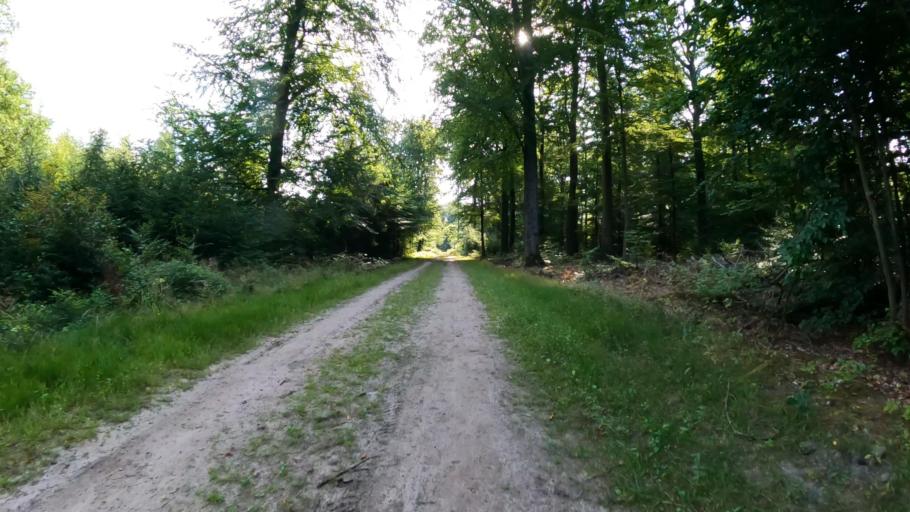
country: DE
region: Schleswig-Holstein
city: Wohltorf
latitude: 53.5008
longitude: 10.3030
